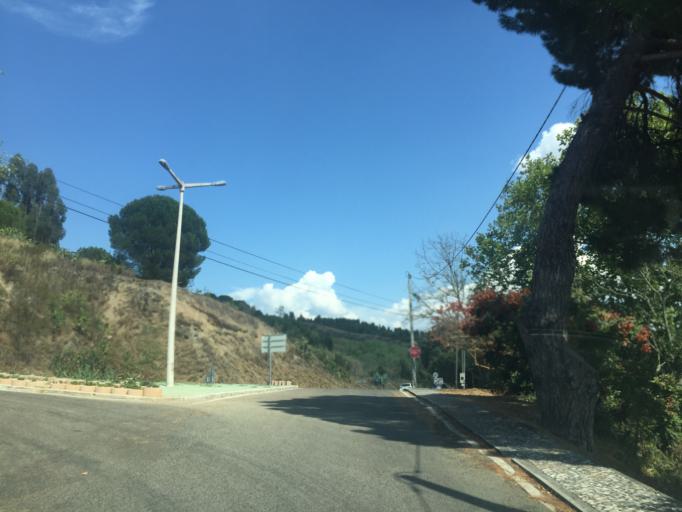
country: PT
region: Santarem
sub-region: Chamusca
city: Vila Nova da Barquinha
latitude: 39.4573
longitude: -8.4197
